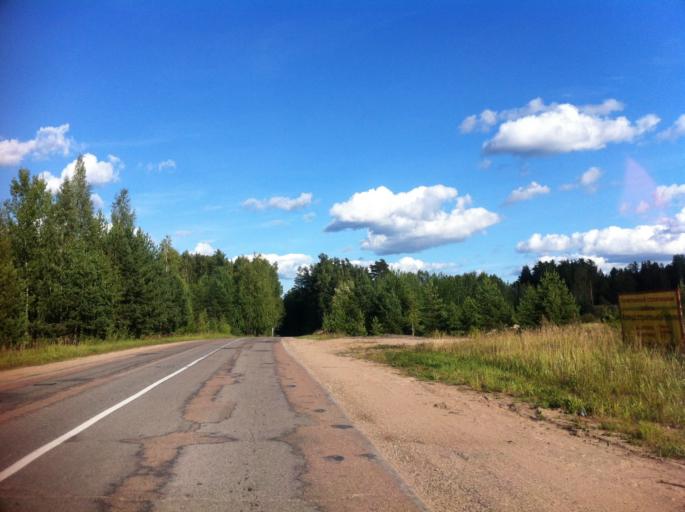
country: RU
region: Pskov
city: Pechory
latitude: 57.8085
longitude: 27.7181
